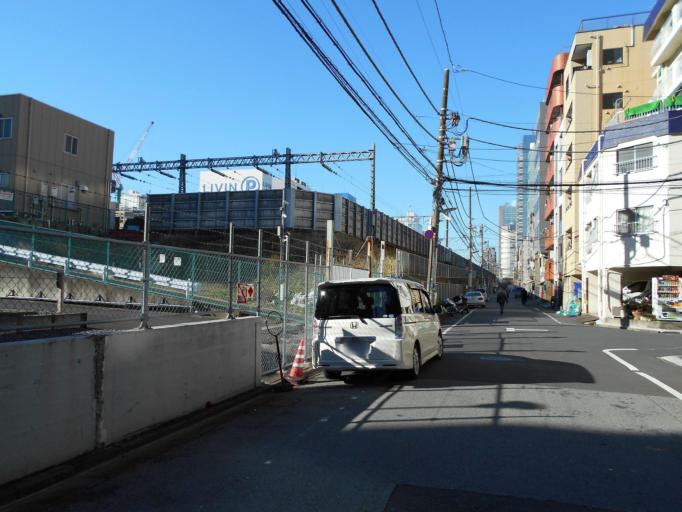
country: JP
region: Tokyo
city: Urayasu
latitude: 35.6974
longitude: 139.8183
